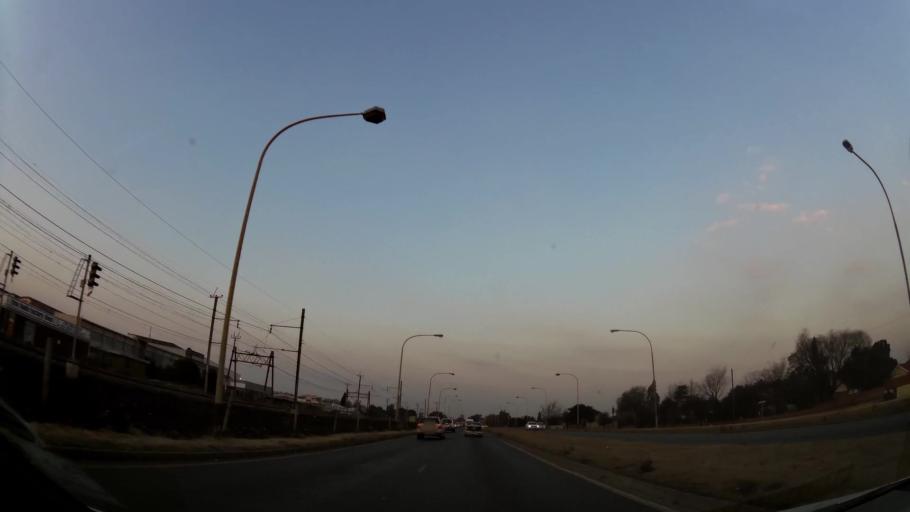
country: ZA
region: Gauteng
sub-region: Ekurhuleni Metropolitan Municipality
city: Springs
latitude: -26.2653
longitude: 28.4231
